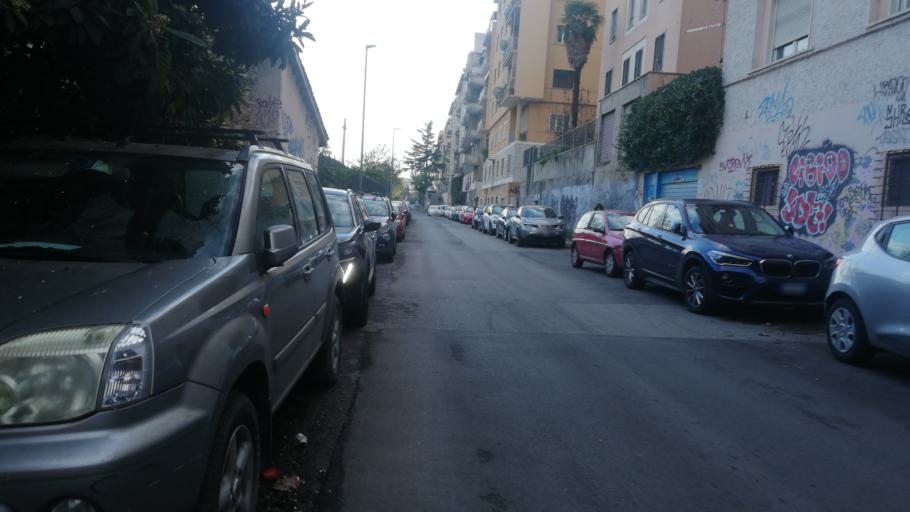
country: IT
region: Latium
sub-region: Citta metropolitana di Roma Capitale
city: Rome
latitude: 41.9324
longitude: 12.5291
